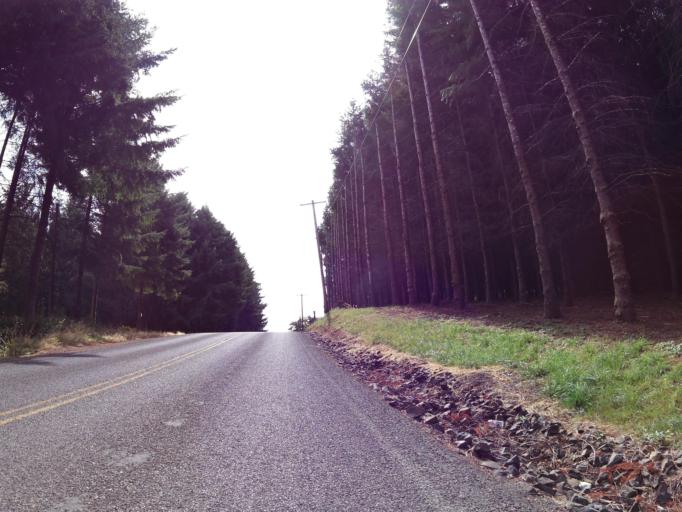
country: US
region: Washington
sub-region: Lewis County
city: Winlock
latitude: 46.5202
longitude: -122.9496
